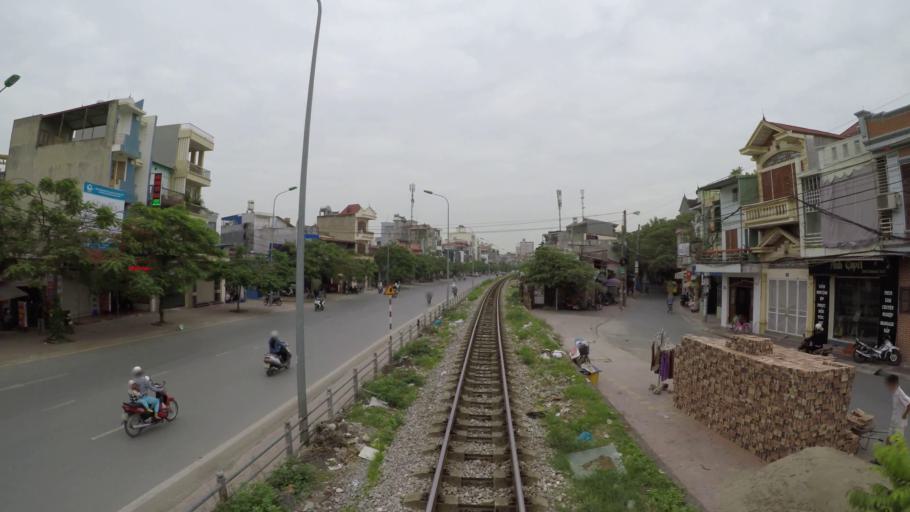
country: VN
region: Hai Phong
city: An Duong
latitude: 20.8746
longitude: 106.6402
